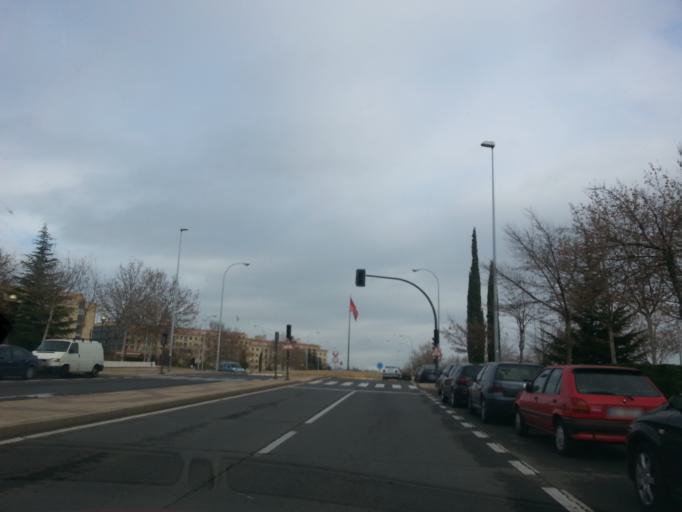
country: ES
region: Castille and Leon
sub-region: Provincia de Salamanca
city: Salamanca
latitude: 40.9767
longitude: -5.6677
